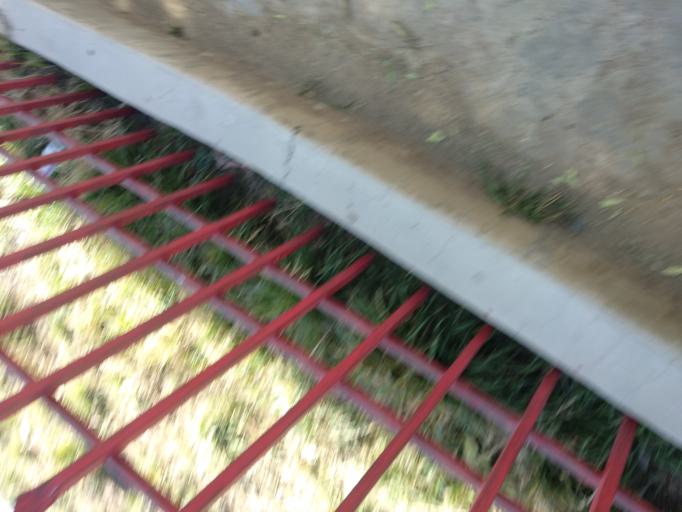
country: BO
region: La Paz
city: La Paz
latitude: -16.5286
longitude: -68.1571
